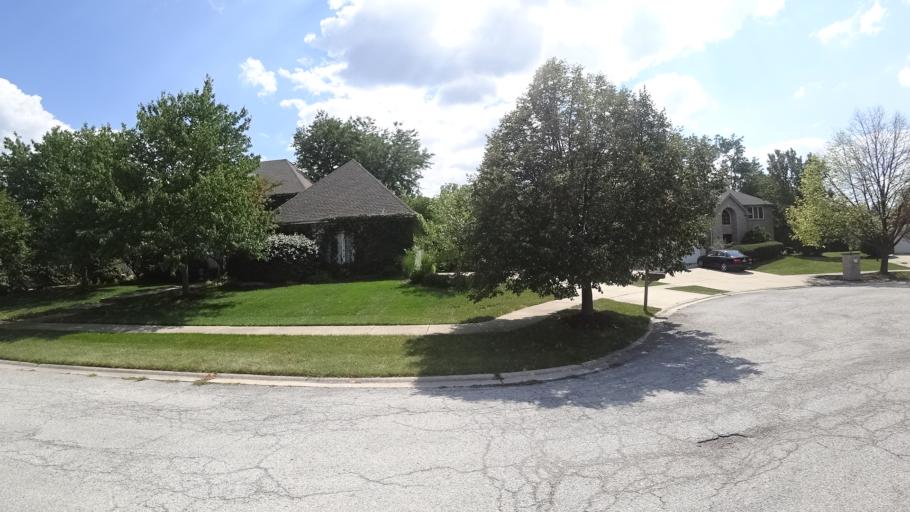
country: US
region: Illinois
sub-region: Cook County
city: Orland Park
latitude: 41.6298
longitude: -87.8164
